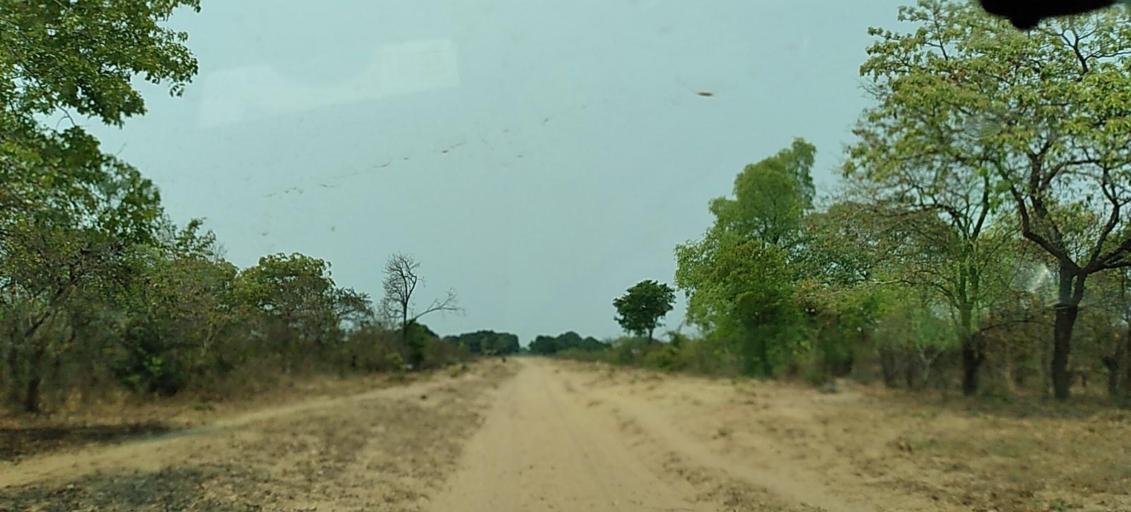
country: ZM
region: Western
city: Lukulu
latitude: -14.1541
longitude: 23.3030
